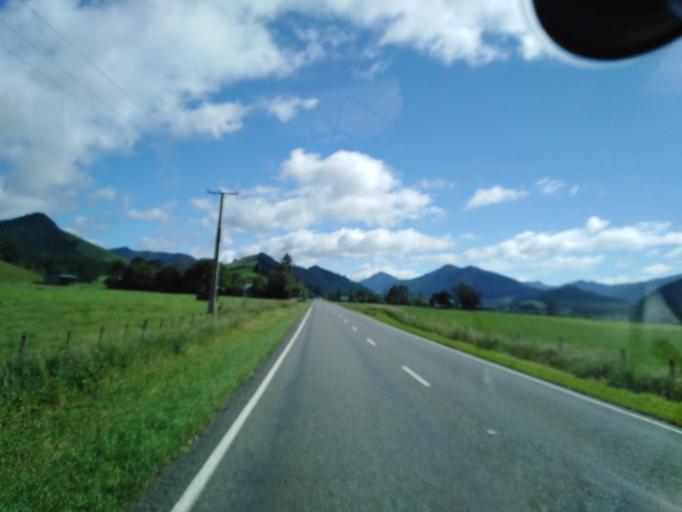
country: NZ
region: Nelson
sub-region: Nelson City
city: Nelson
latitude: -41.2423
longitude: 173.5783
